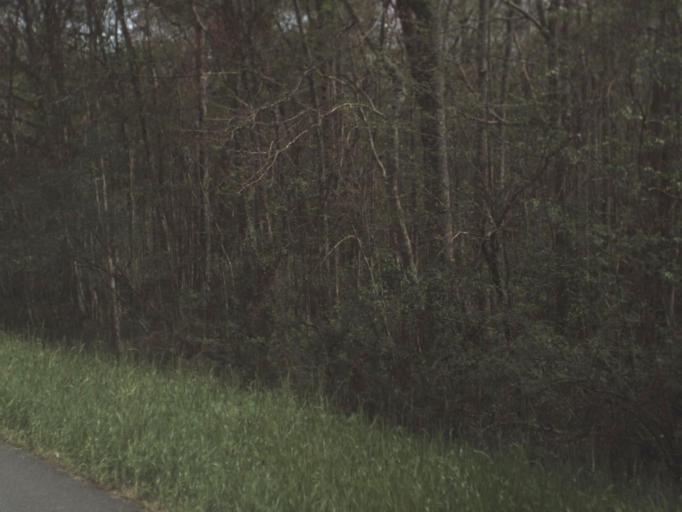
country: US
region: Florida
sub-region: Jackson County
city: Malone
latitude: 30.9465
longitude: -85.2634
